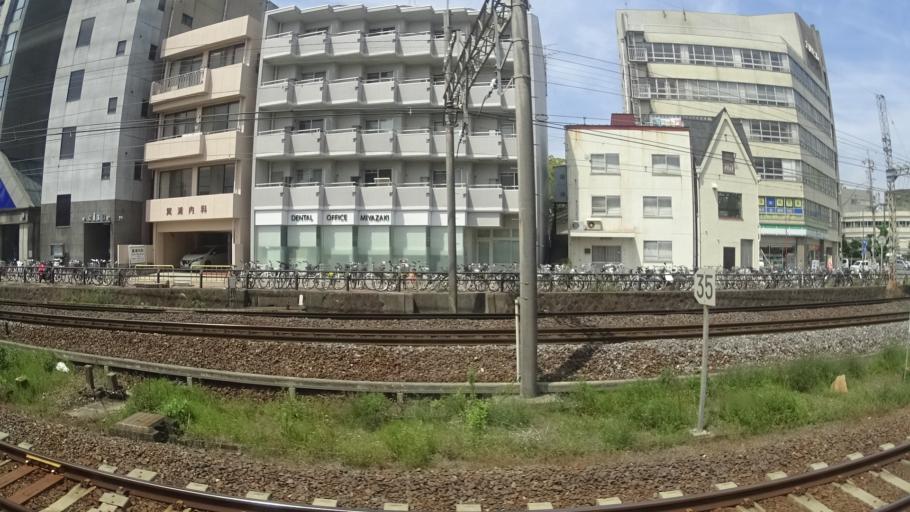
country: JP
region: Mie
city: Tsu-shi
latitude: 34.7323
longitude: 136.5107
